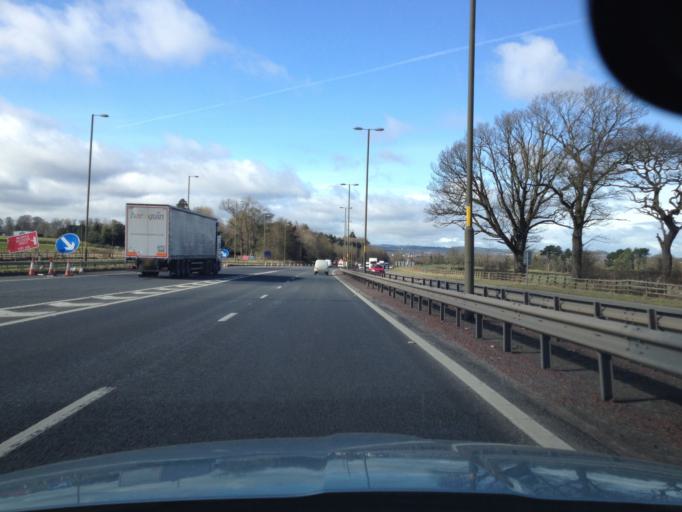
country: GB
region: Scotland
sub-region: Edinburgh
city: Newbridge
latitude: 55.9252
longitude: -3.4175
